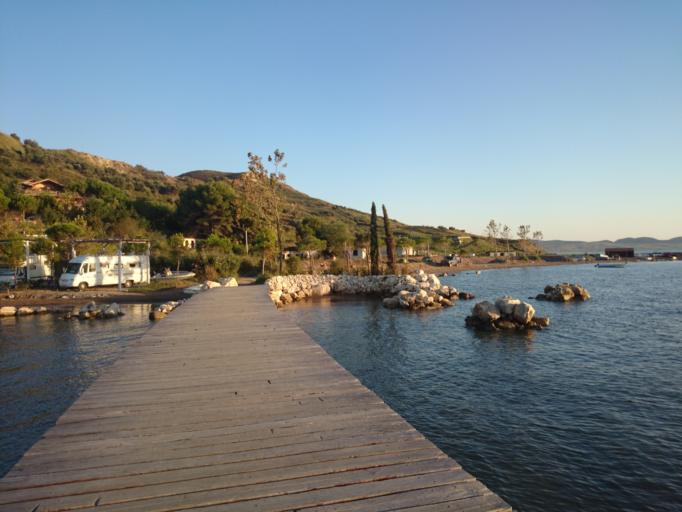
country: AL
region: Tirane
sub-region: Rrethi i Tiranes
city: Shengjergj
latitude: 41.1825
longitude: 19.4767
